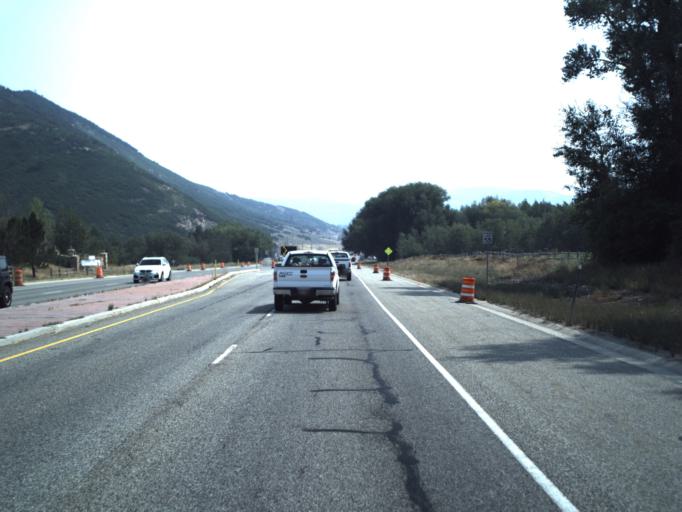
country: US
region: Utah
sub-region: Summit County
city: Snyderville
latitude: 40.6853
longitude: -111.5415
